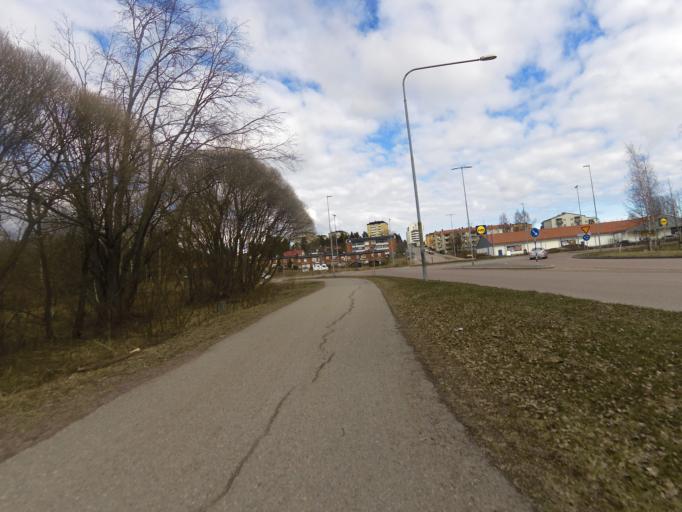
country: SE
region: Gaevleborg
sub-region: Gavle Kommun
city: Gavle
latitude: 60.6926
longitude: 17.1483
